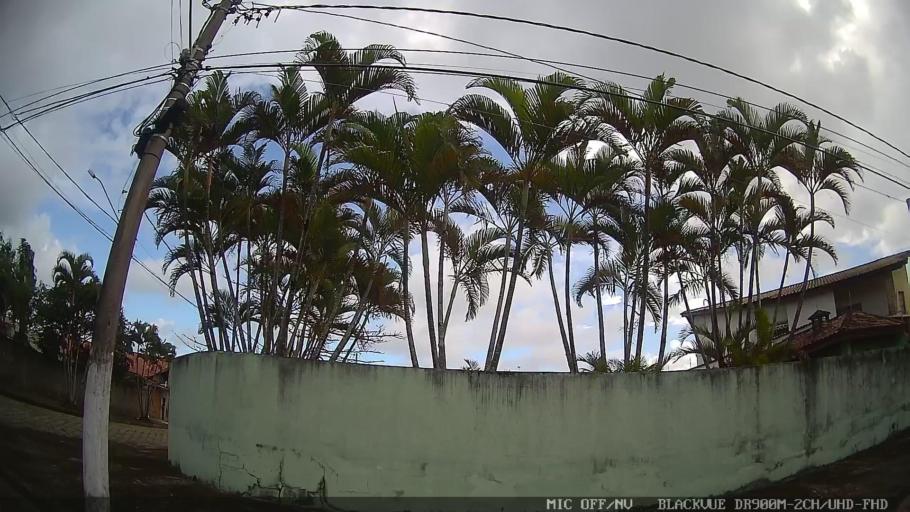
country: BR
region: Sao Paulo
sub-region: Itanhaem
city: Itanhaem
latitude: -24.2189
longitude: -46.8503
